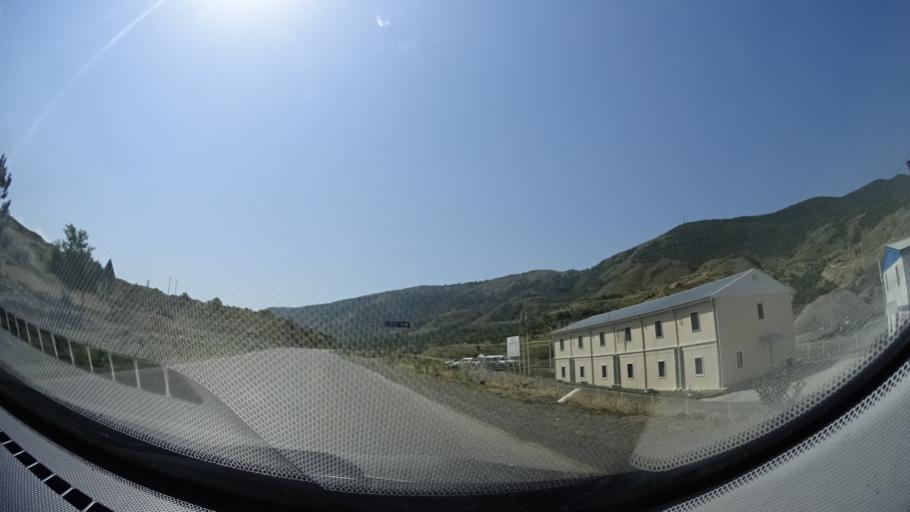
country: GE
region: Samtskhe-Javakheti
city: Aspindza
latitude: 41.6026
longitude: 43.1473
